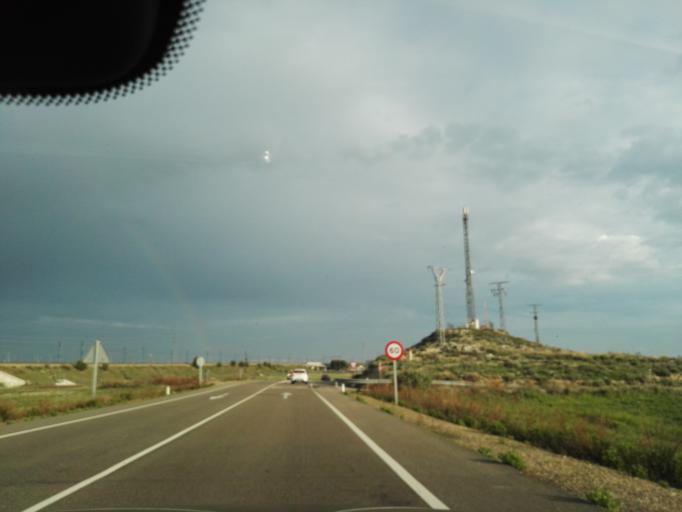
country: ES
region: Aragon
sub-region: Provincia de Zaragoza
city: Montecanal
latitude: 41.6256
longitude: -0.9878
